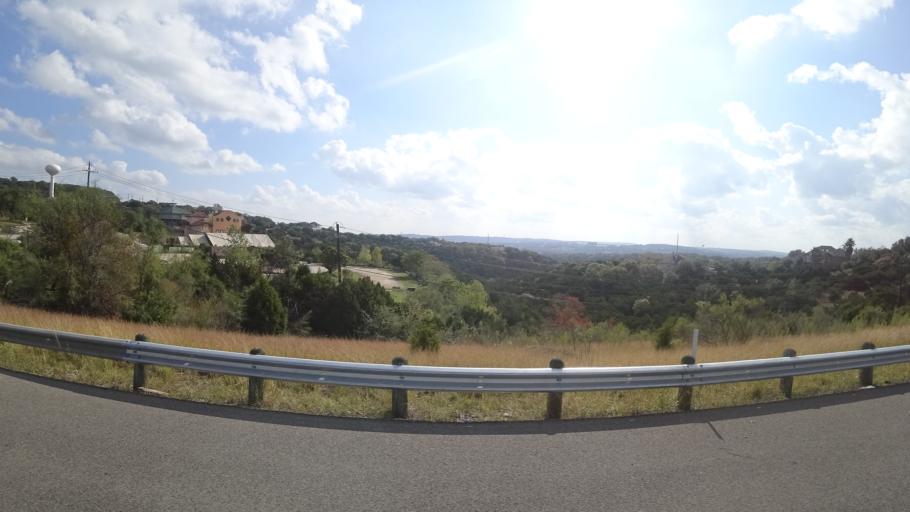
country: US
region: Texas
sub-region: Travis County
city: Lost Creek
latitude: 30.3101
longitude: -97.8462
